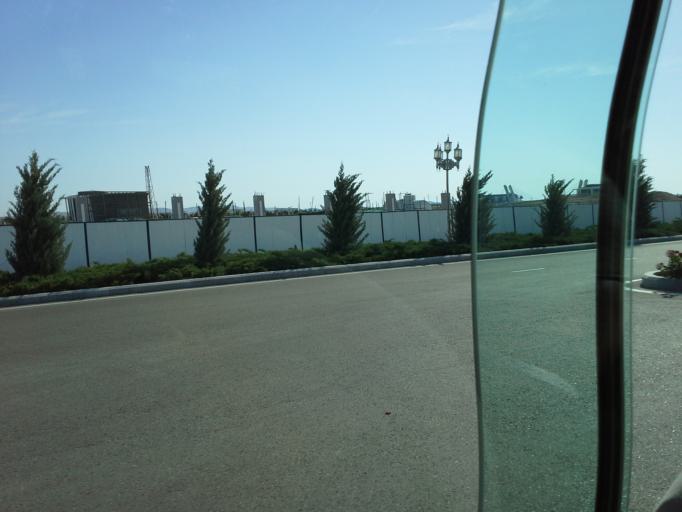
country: TM
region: Balkan
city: Turkmenbasy
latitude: 39.9618
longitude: 52.8380
